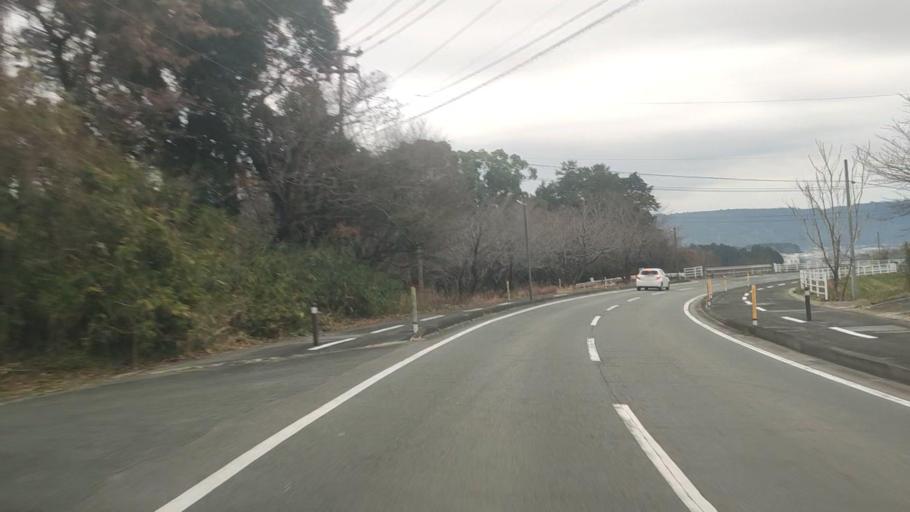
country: JP
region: Kumamoto
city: Ozu
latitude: 32.8722
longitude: 130.8942
